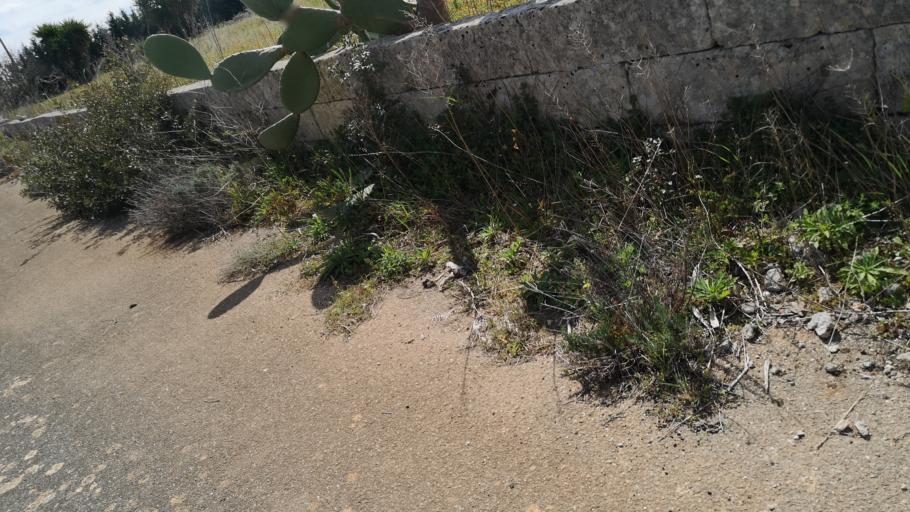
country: IT
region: Apulia
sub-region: Provincia di Lecce
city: Spongano
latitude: 40.0313
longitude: 18.3642
